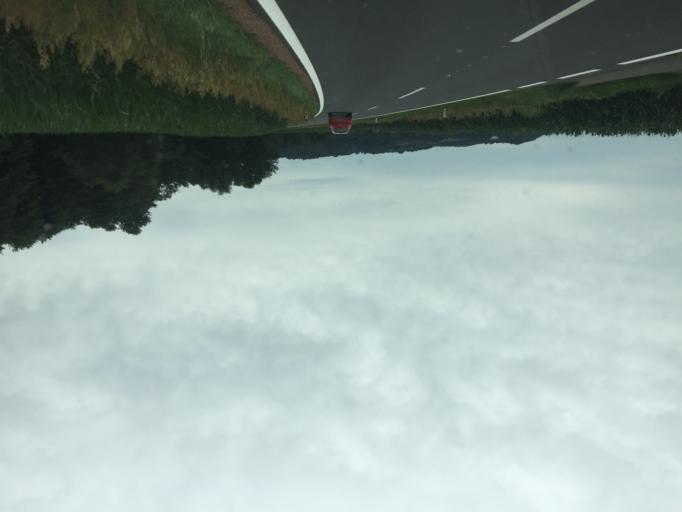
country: AT
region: Styria
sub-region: Politischer Bezirk Suedoststeiermark
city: Eichfeld
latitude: 46.7116
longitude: 15.7432
